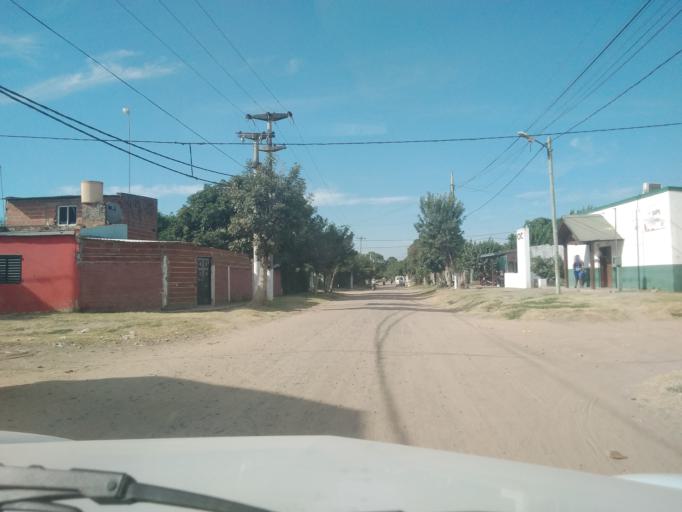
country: AR
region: Corrientes
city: Corrientes
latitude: -27.5076
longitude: -58.8052
